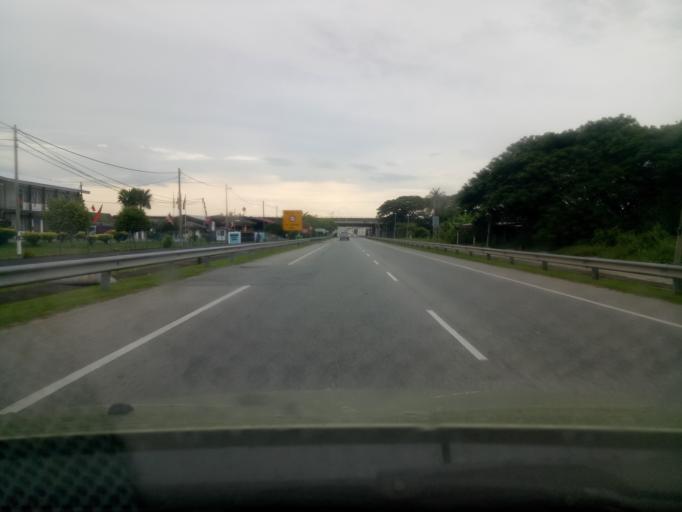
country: MY
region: Kedah
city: Gurun
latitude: 5.9740
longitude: 100.4453
